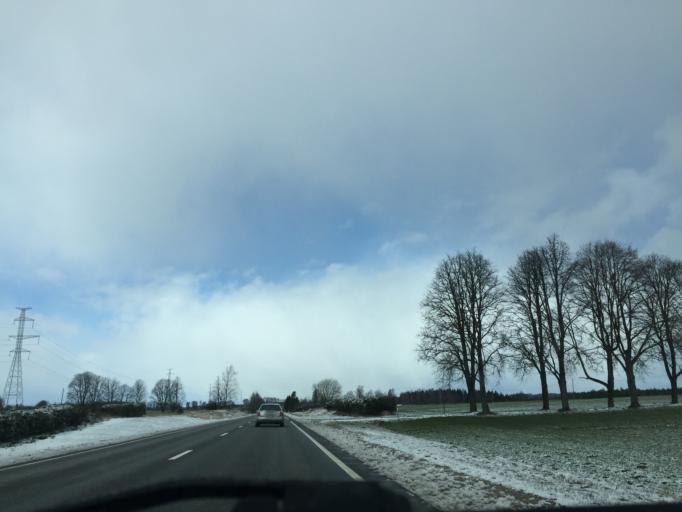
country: LV
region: Kandava
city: Kandava
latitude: 57.1185
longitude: 22.7488
